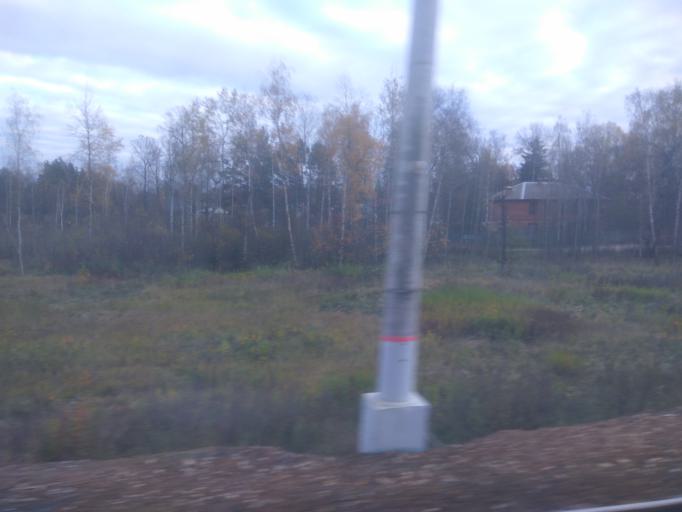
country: RU
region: Moskovskaya
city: Aprelevka
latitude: 55.5686
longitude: 37.0946
